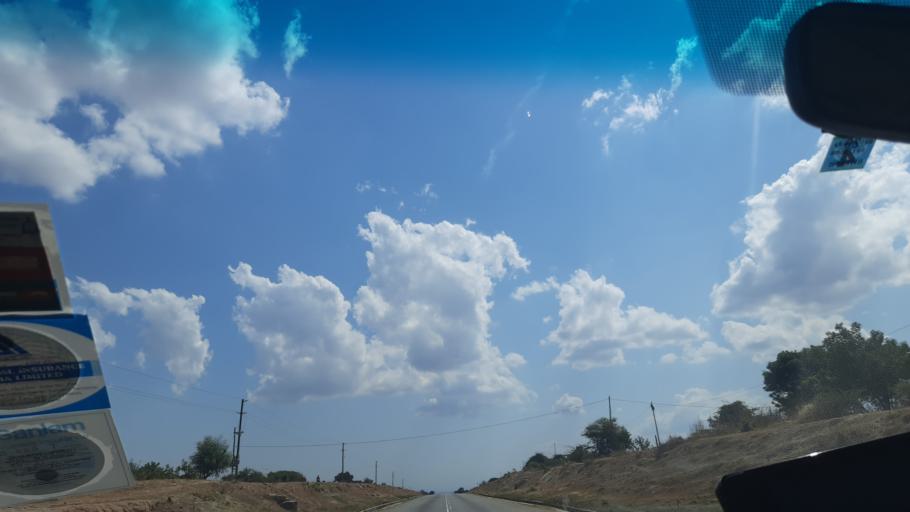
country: TZ
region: Singida
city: Kintinku
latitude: -6.0167
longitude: 35.4472
